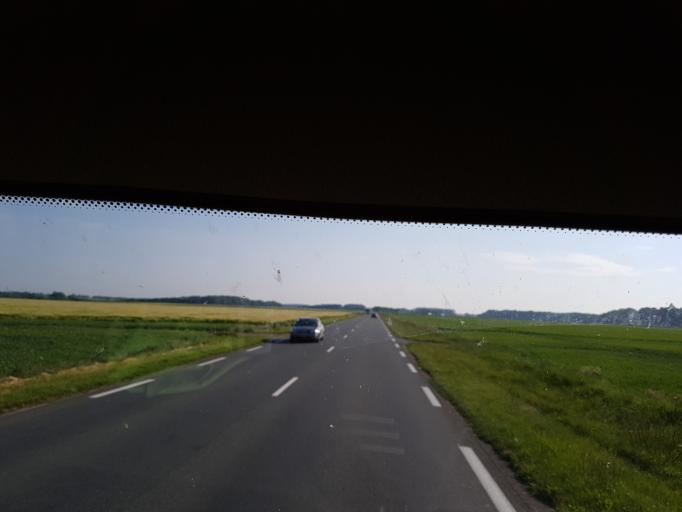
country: FR
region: Picardie
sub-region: Departement de la Somme
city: Crecy-en-Ponthieu
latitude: 50.2040
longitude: 1.8976
